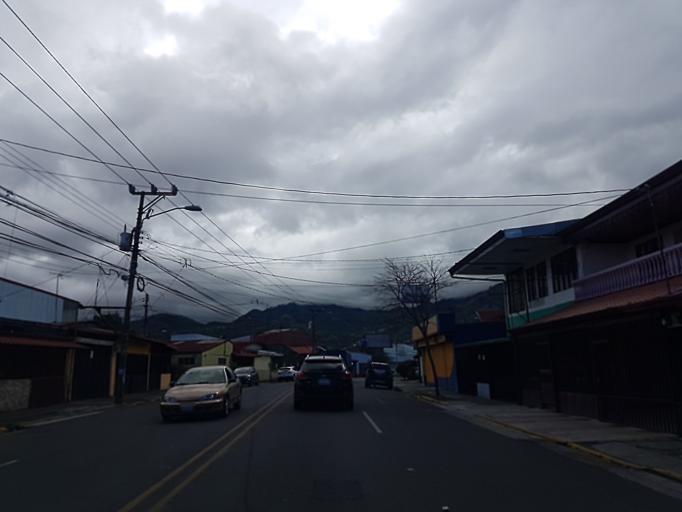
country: CR
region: San Jose
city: San Felipe
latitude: 9.9174
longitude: -84.1011
